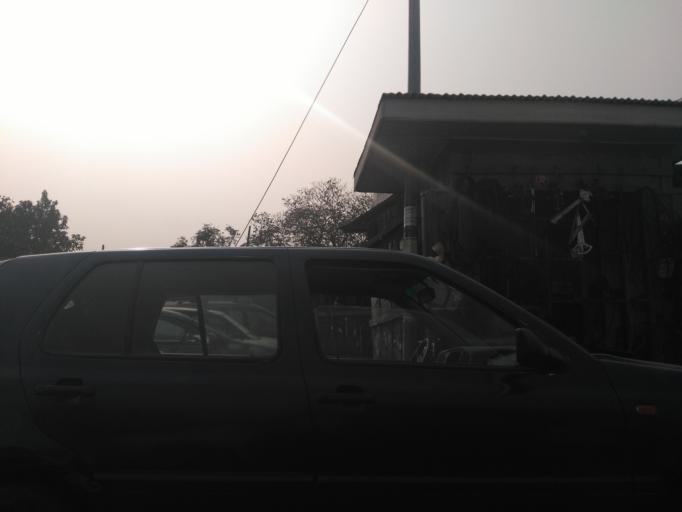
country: GH
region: Ashanti
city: Kumasi
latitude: 6.6852
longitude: -1.6095
